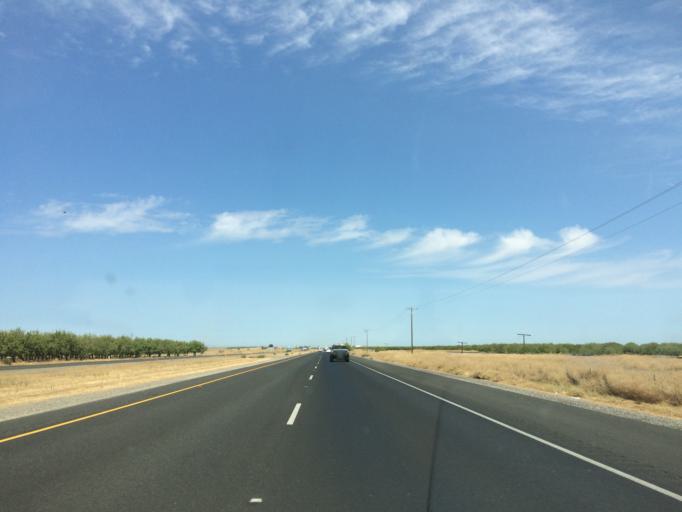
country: US
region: California
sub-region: Yolo County
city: Dunnigan
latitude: 38.9379
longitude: -122.0049
